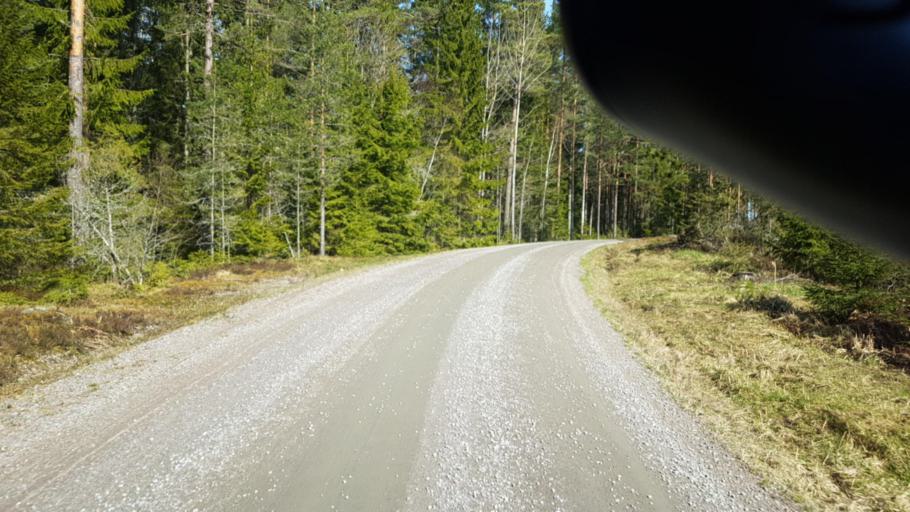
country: SE
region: Vaermland
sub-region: Arvika Kommun
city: Arvika
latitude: 59.5624
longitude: 12.7411
